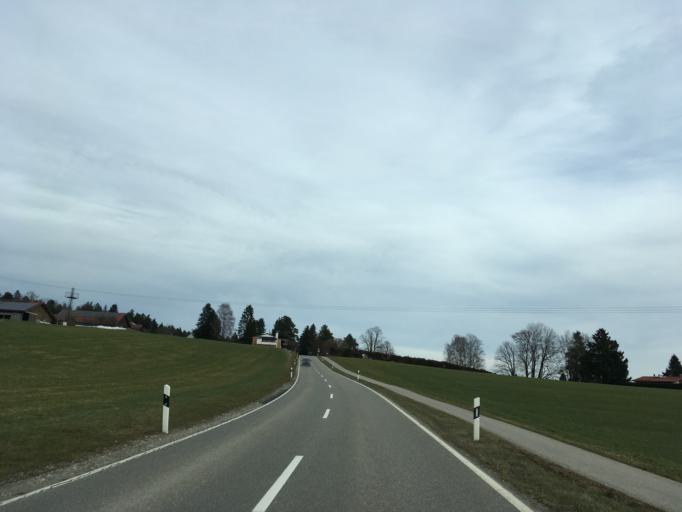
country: DE
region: Bavaria
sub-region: Upper Bavaria
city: Eggstatt
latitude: 47.8917
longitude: 12.3734
